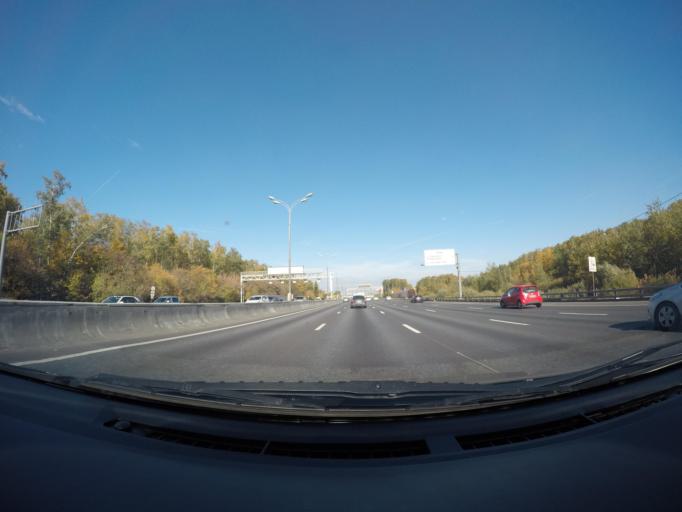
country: RU
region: Moskovskaya
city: Kuskovo
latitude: 55.7204
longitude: 37.8393
